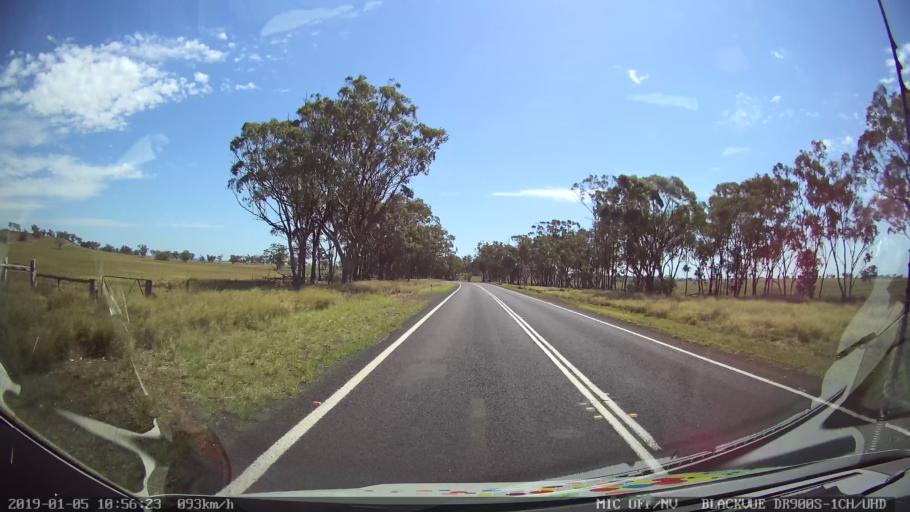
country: AU
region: New South Wales
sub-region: Warrumbungle Shire
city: Coonabarabran
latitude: -31.4418
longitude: 149.1574
